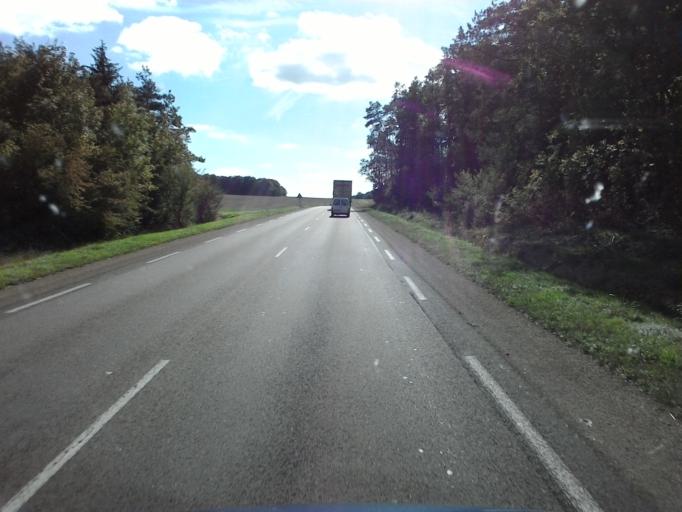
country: FR
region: Bourgogne
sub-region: Departement de la Cote-d'Or
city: Chatillon-sur-Seine
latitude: 47.7924
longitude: 4.5165
